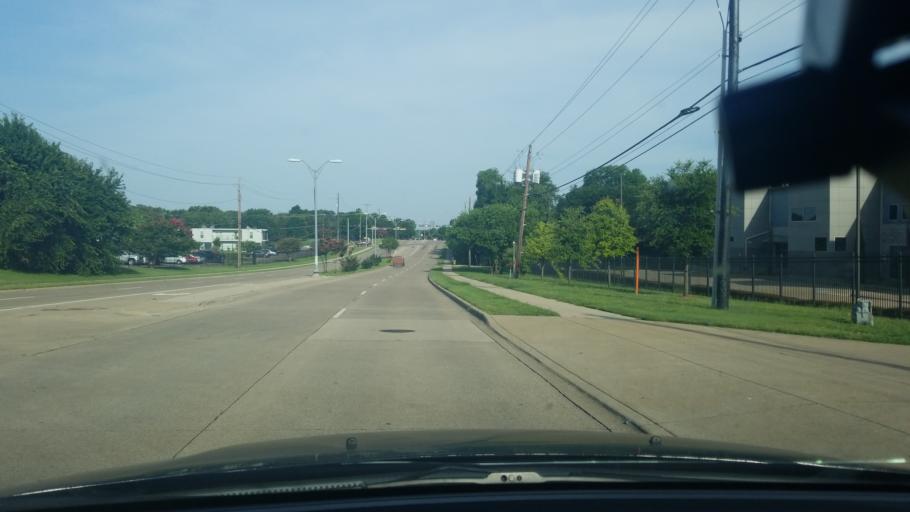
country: US
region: Texas
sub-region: Dallas County
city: Highland Park
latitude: 32.7924
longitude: -96.7098
